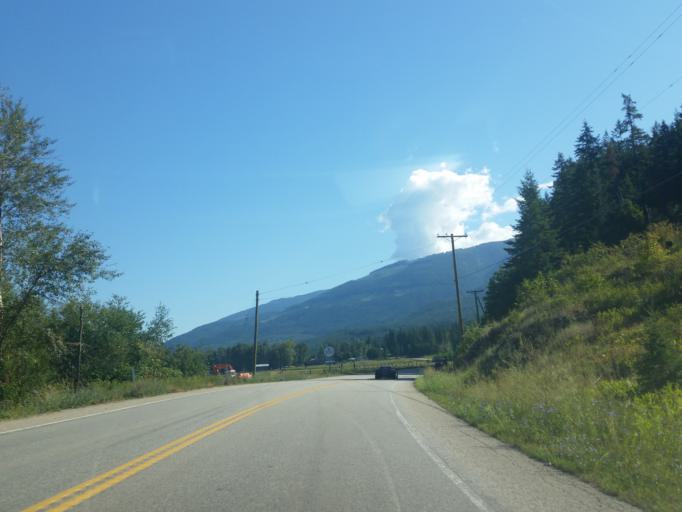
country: CA
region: British Columbia
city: Enderby
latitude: 50.6631
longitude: -119.0733
